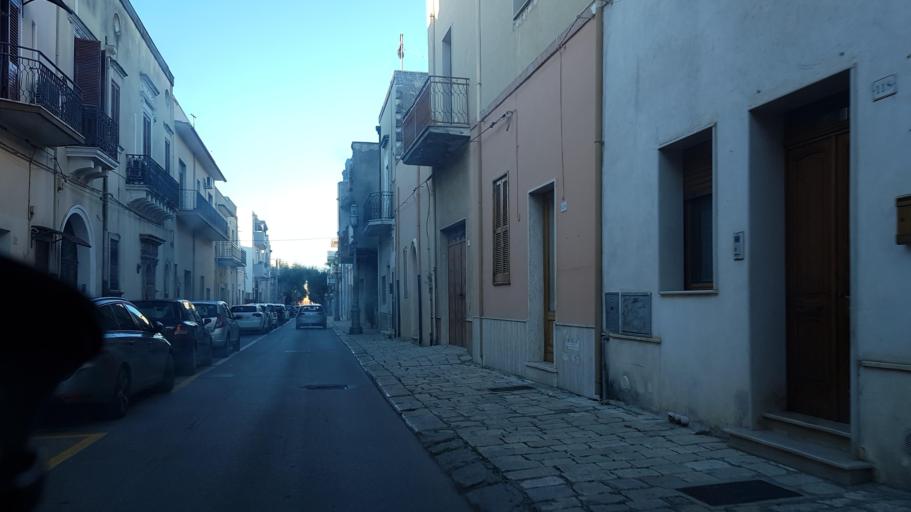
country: IT
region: Apulia
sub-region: Provincia di Brindisi
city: Latiano
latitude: 40.5550
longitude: 17.7187
